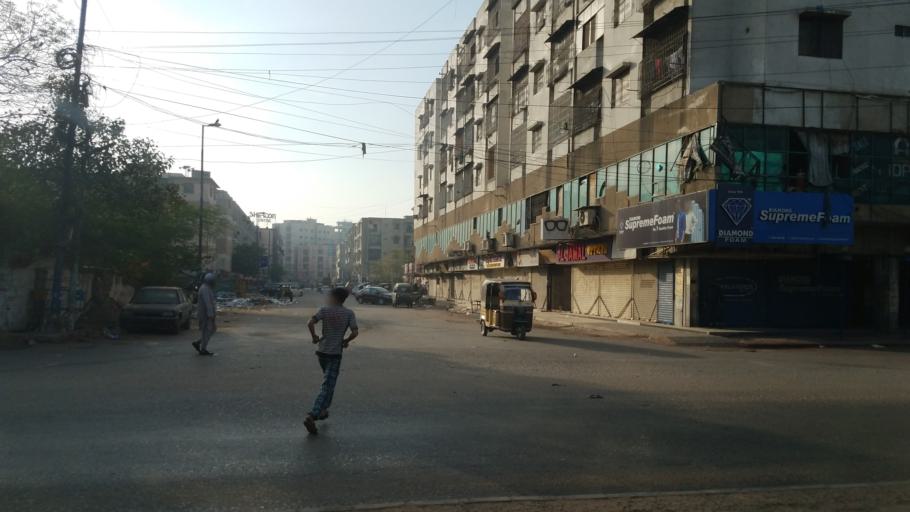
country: PK
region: Sindh
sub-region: Karachi District
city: Karachi
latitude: 24.9286
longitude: 67.0663
